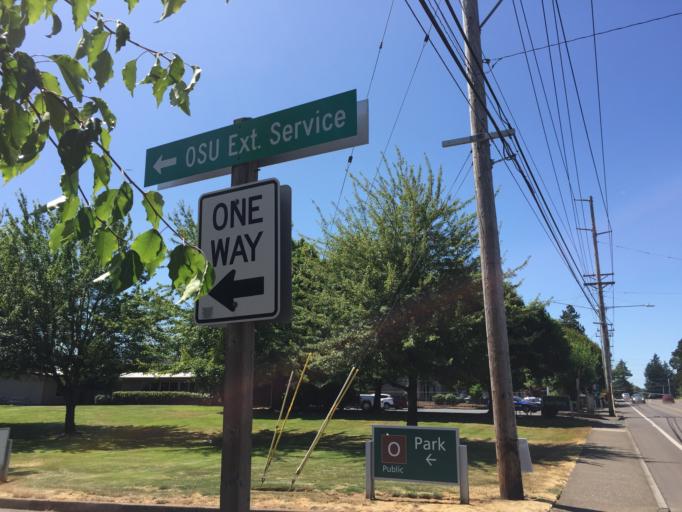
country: US
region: Oregon
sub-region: Clackamas County
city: Oregon City
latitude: 45.3364
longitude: -122.6006
